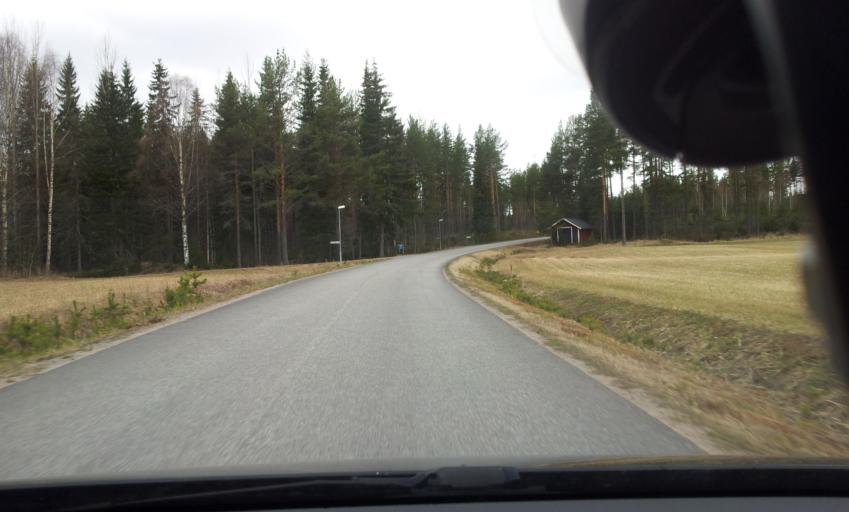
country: SE
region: Gaevleborg
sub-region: Ljusdals Kommun
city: Farila
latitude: 61.8073
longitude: 15.8945
